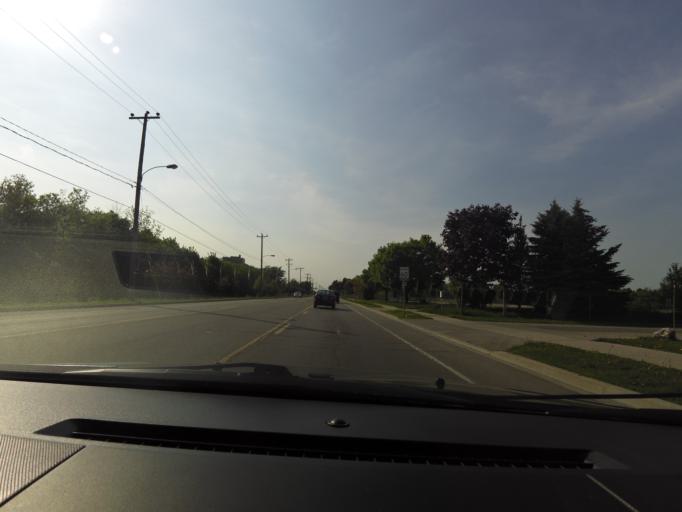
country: CA
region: Ontario
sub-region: Wellington County
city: Guelph
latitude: 43.5445
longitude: -80.2677
